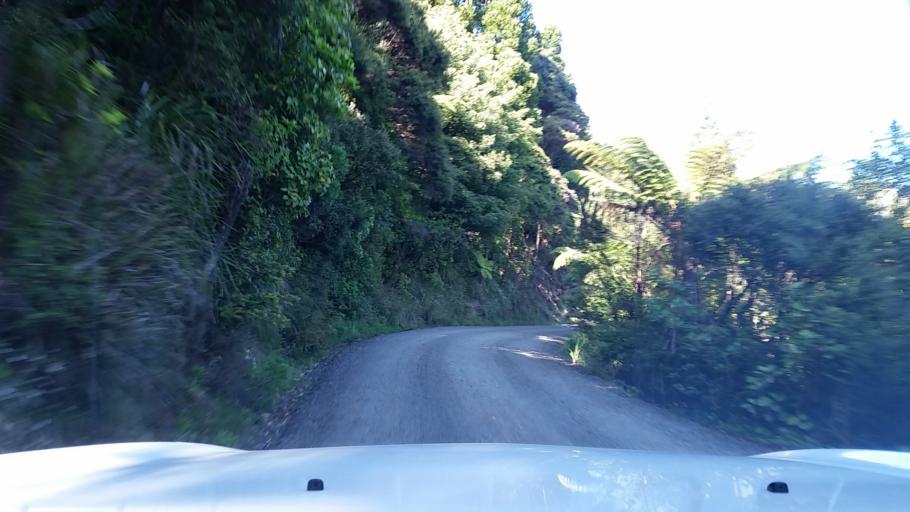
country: NZ
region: Auckland
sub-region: Auckland
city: Titirangi
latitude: -37.0197
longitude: 174.5475
